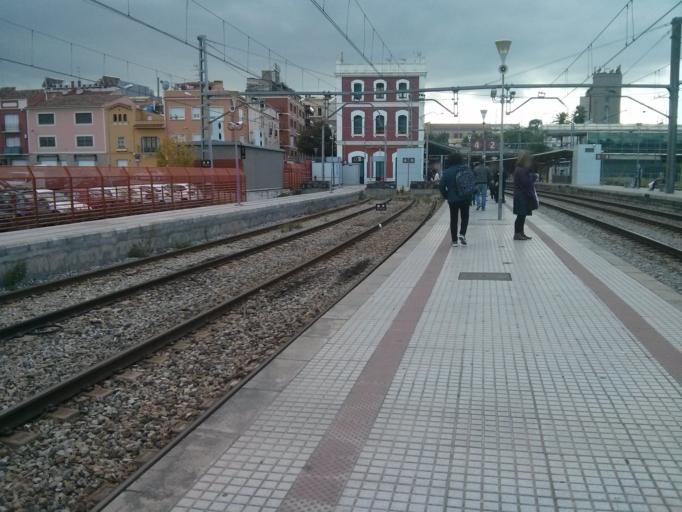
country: ES
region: Catalonia
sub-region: Provincia de Barcelona
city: Martorell
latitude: 41.4793
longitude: 1.9274
